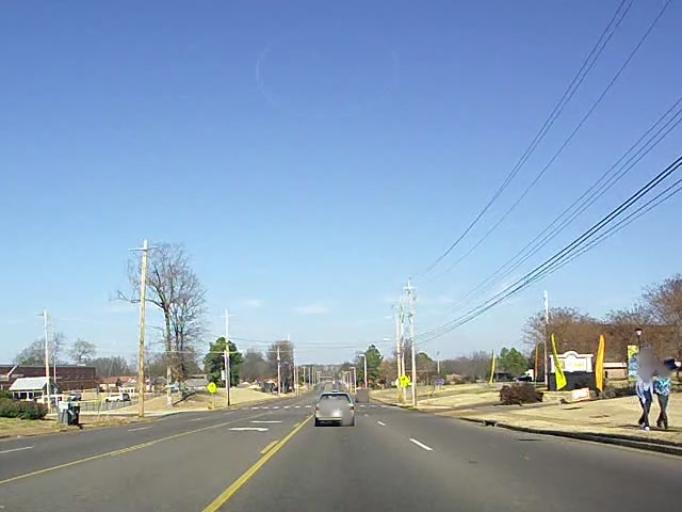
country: US
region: Tennessee
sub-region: Shelby County
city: Germantown
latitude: 35.0622
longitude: -89.8569
